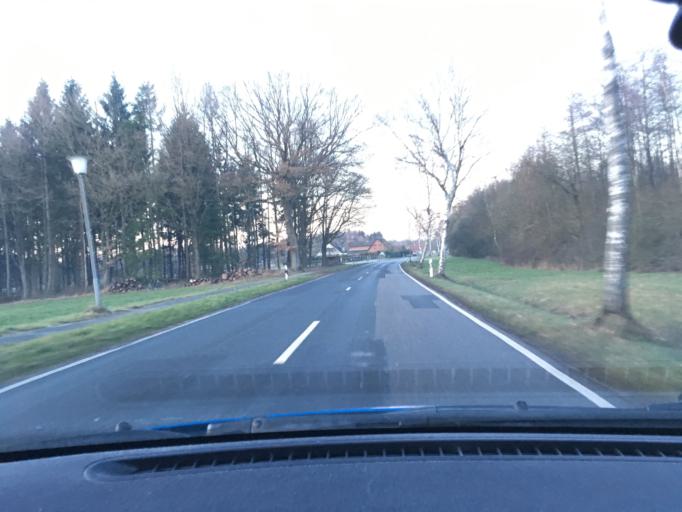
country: DE
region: Lower Saxony
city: Handeloh
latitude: 53.2570
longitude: 9.8827
